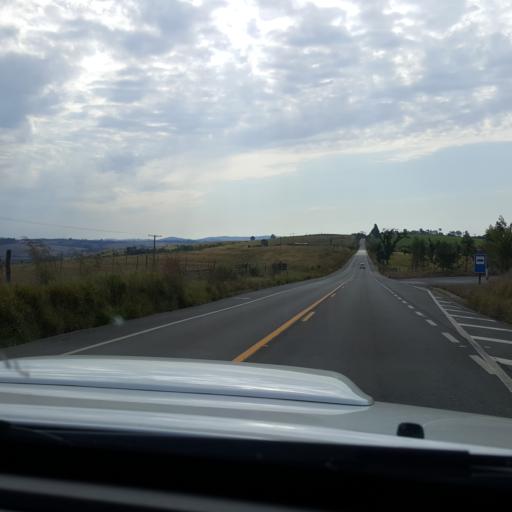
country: BR
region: Sao Paulo
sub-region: Itaporanga
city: Itaporanga
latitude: -23.7615
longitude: -49.4487
